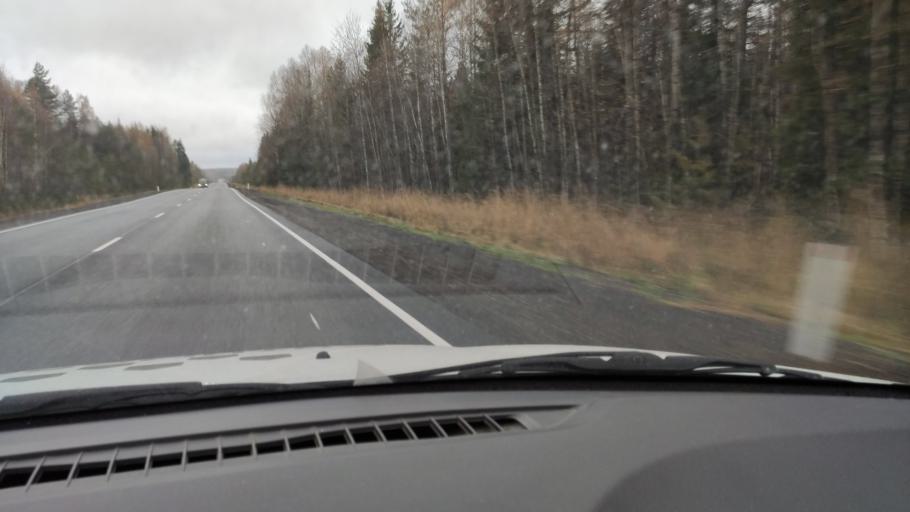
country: RU
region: Kirov
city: Chernaya Kholunitsa
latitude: 58.8865
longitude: 51.3896
